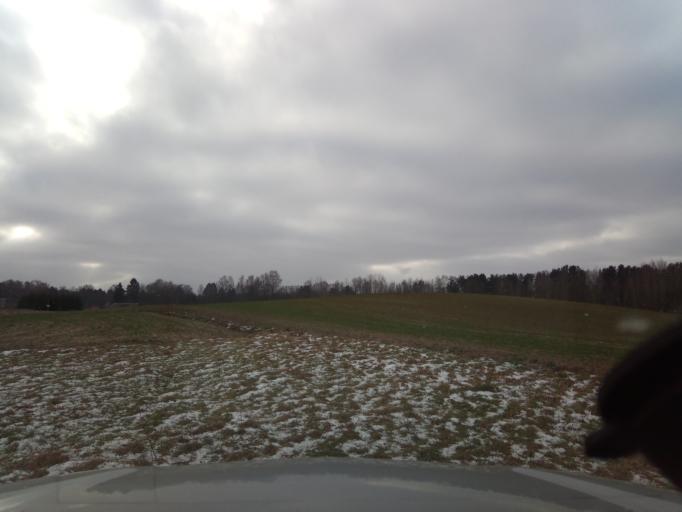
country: LT
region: Alytaus apskritis
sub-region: Alytaus rajonas
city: Daugai
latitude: 54.3175
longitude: 24.3698
